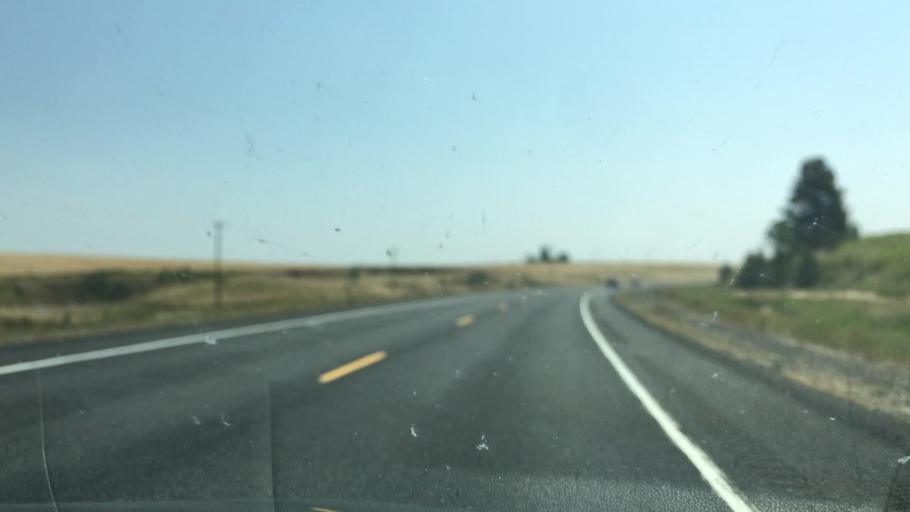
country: US
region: Idaho
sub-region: Lewis County
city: Nezperce
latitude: 46.2282
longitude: -116.4438
